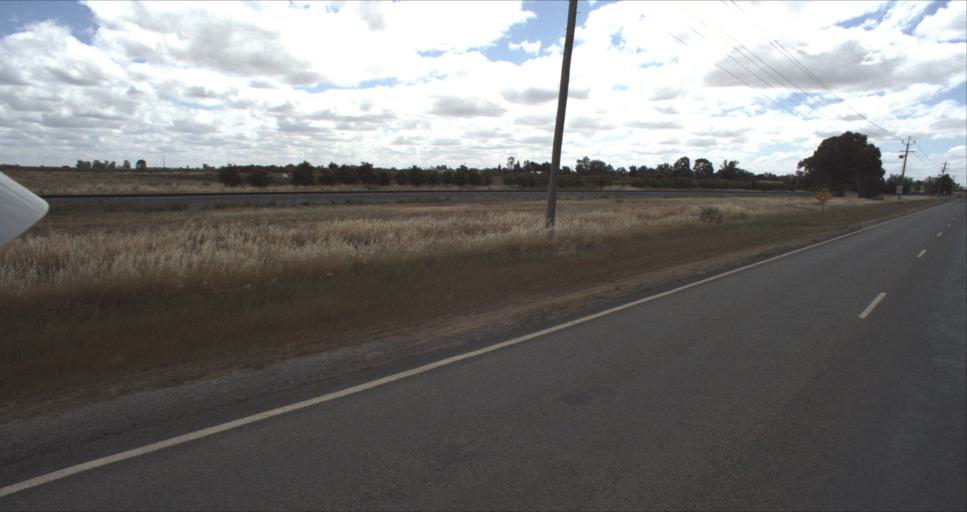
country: AU
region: New South Wales
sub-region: Leeton
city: Leeton
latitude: -34.5739
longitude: 146.3949
